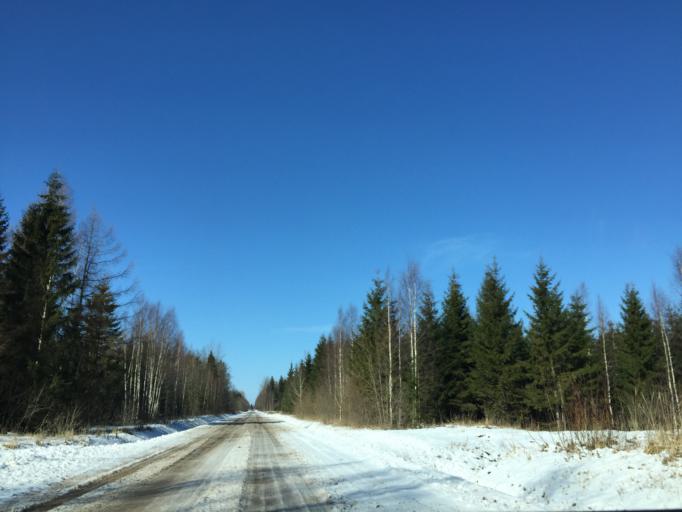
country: LV
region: Salacgrivas
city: Ainazi
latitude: 58.0298
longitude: 24.5216
